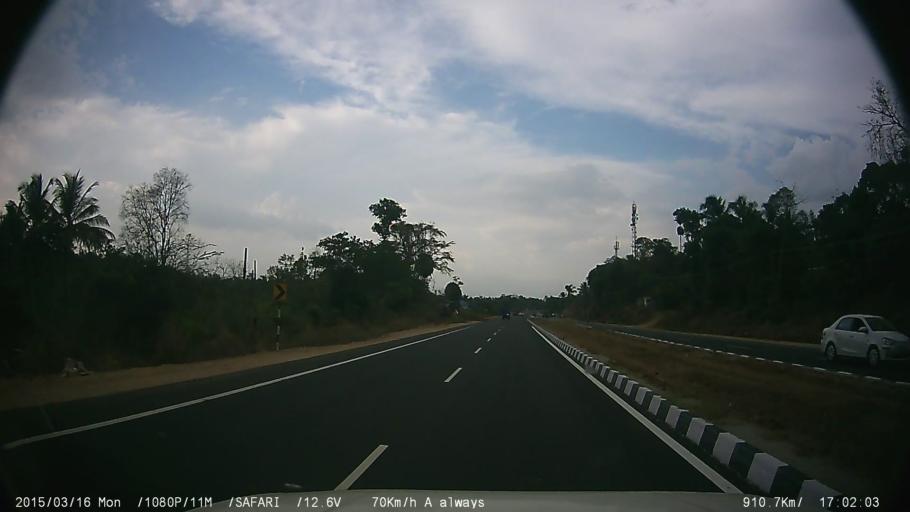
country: IN
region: Kerala
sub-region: Palakkad district
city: Palakkad
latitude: 10.6812
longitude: 76.5785
